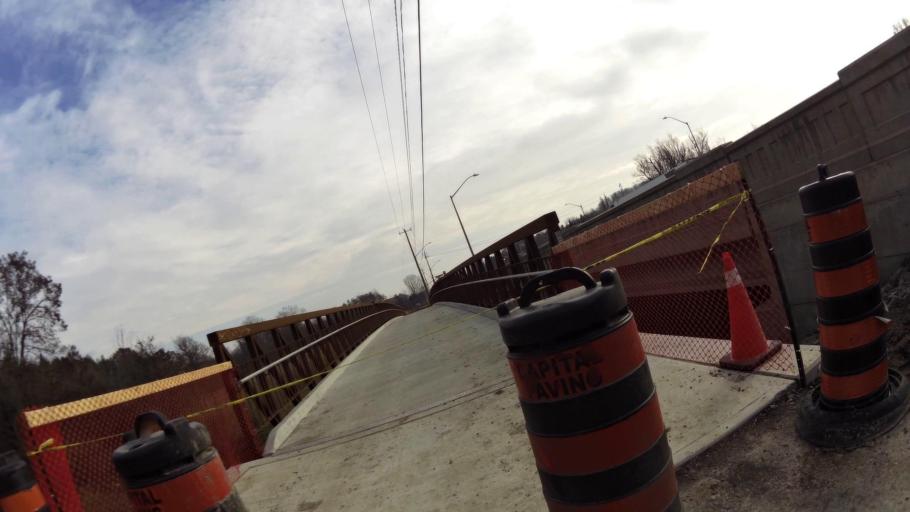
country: CA
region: Ontario
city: Kitchener
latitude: 43.3902
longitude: -80.4229
